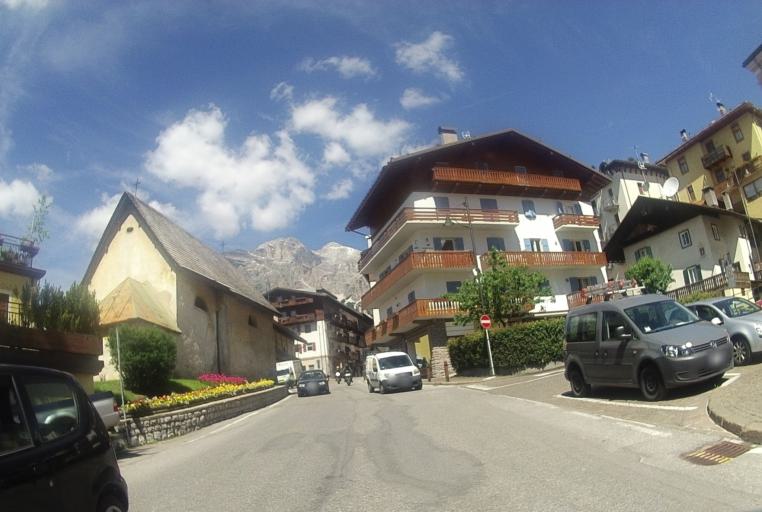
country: IT
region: Veneto
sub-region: Provincia di Belluno
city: Cortina d'Ampezzo
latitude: 46.5362
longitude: 12.1384
